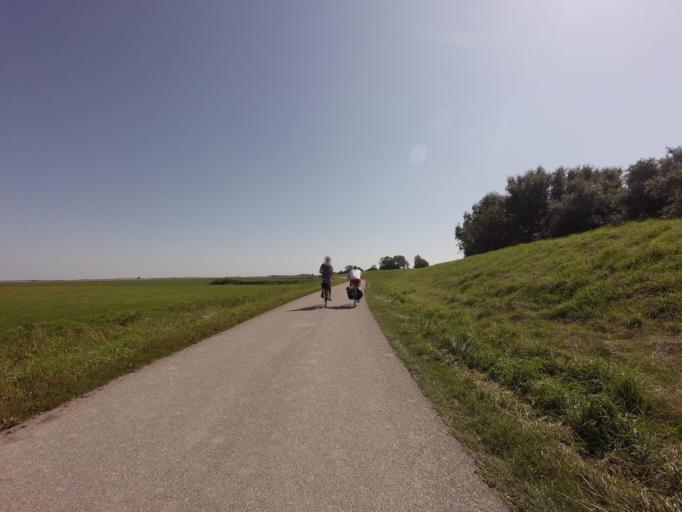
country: NL
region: Friesland
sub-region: Gemeente Dongeradeel
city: Anjum
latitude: 53.3943
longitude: 6.1118
